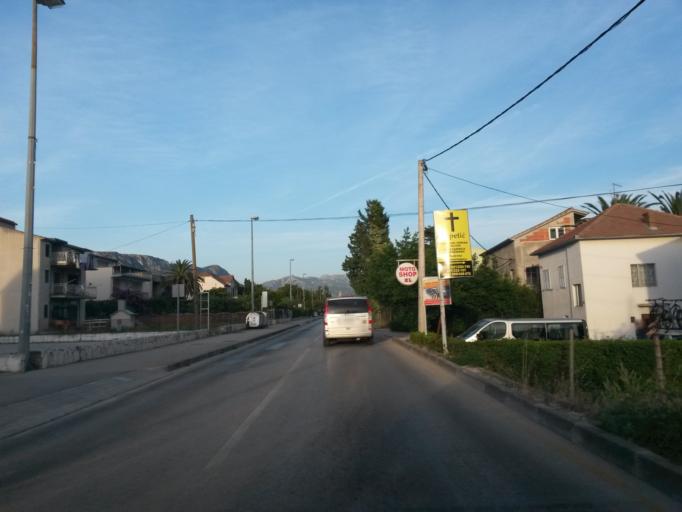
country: HR
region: Splitsko-Dalmatinska
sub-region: Grad Split
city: Split
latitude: 43.5498
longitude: 16.3877
